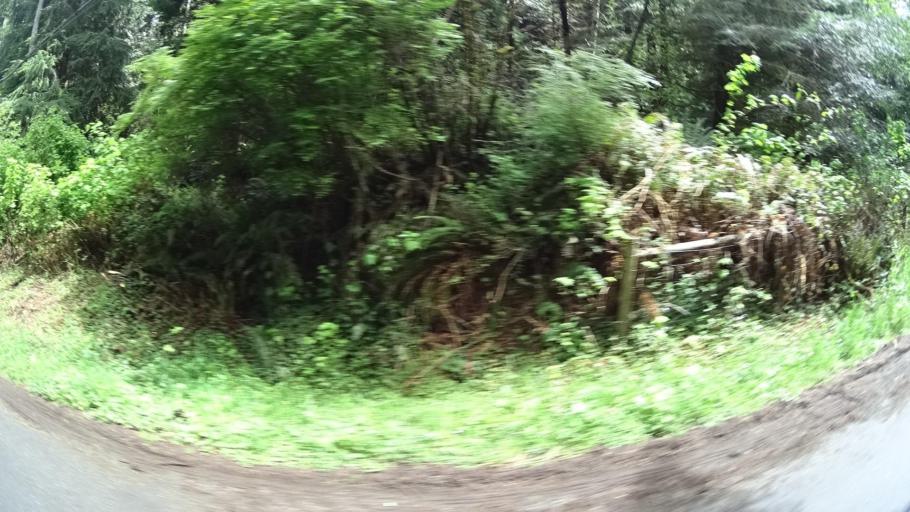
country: US
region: California
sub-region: Humboldt County
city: Bayside
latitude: 40.8318
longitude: -124.0126
